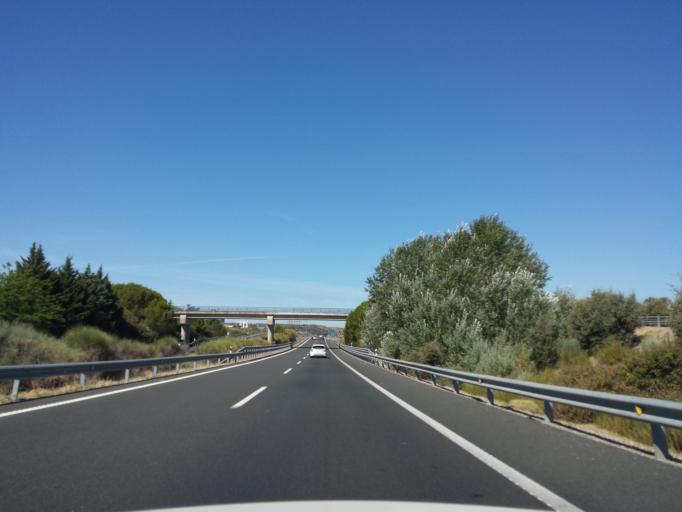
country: ES
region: Extremadura
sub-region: Provincia de Caceres
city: Peraleda de la Mata
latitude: 39.8896
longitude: -5.4652
